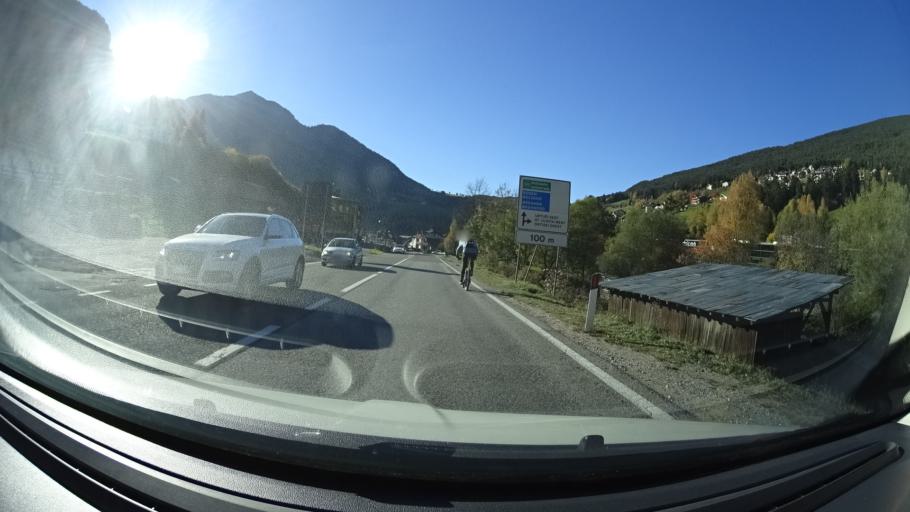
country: IT
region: Trentino-Alto Adige
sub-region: Bolzano
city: Ortisei
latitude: 46.5737
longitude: 11.6591
